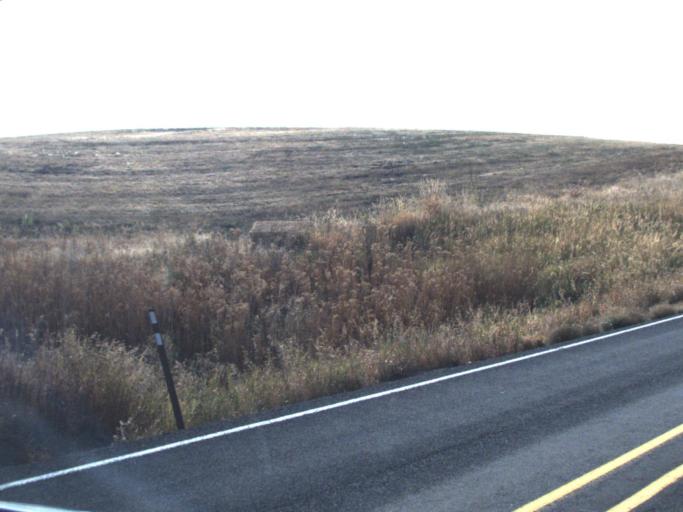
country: US
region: Idaho
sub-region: Benewah County
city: Plummer
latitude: 47.2377
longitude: -117.1195
